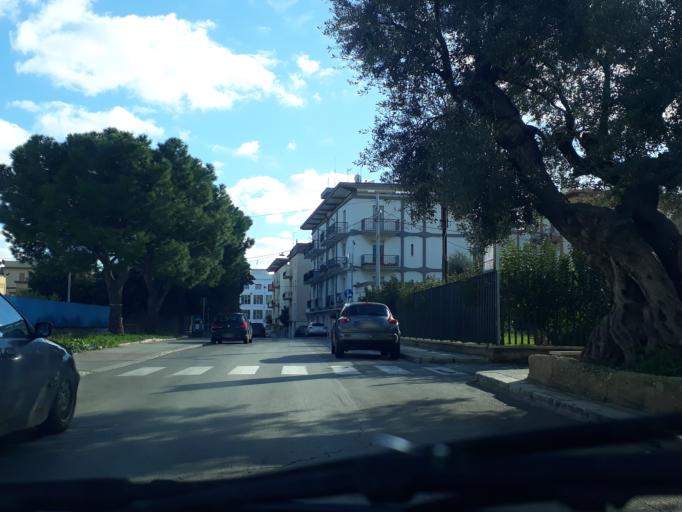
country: IT
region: Apulia
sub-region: Provincia di Brindisi
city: Fasano
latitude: 40.8355
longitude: 17.3541
